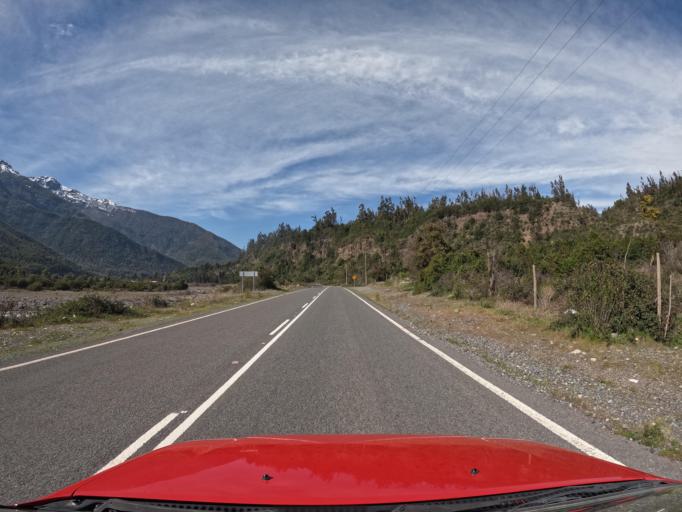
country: CL
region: Maule
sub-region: Provincia de Curico
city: Teno
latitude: -35.0039
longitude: -70.8297
